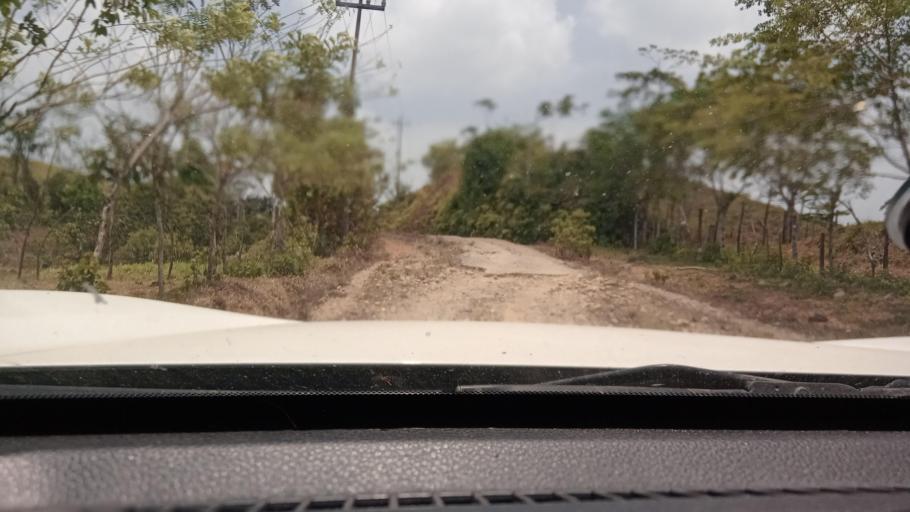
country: MX
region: Tabasco
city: Chontalpa
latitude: 17.5583
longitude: -93.7278
